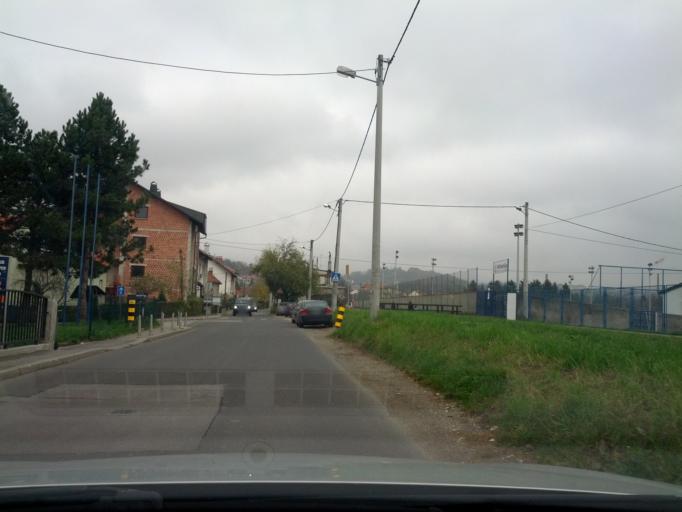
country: HR
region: Grad Zagreb
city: Jankomir
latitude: 45.8084
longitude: 15.9247
